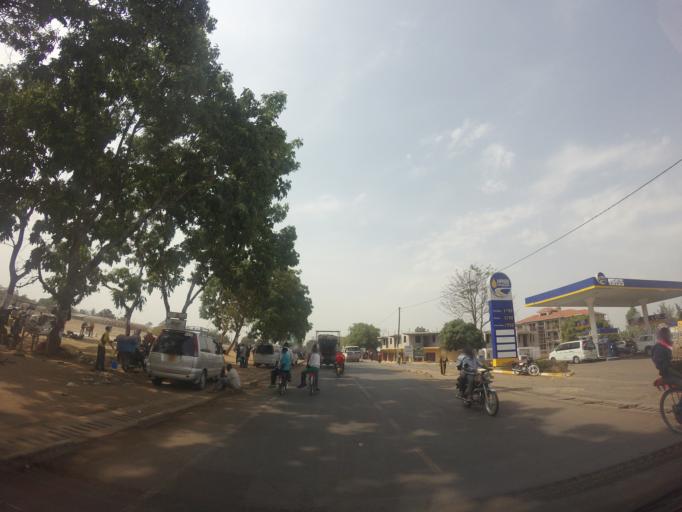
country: UG
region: Northern Region
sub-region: Arua District
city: Arua
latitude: 3.0138
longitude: 30.9143
